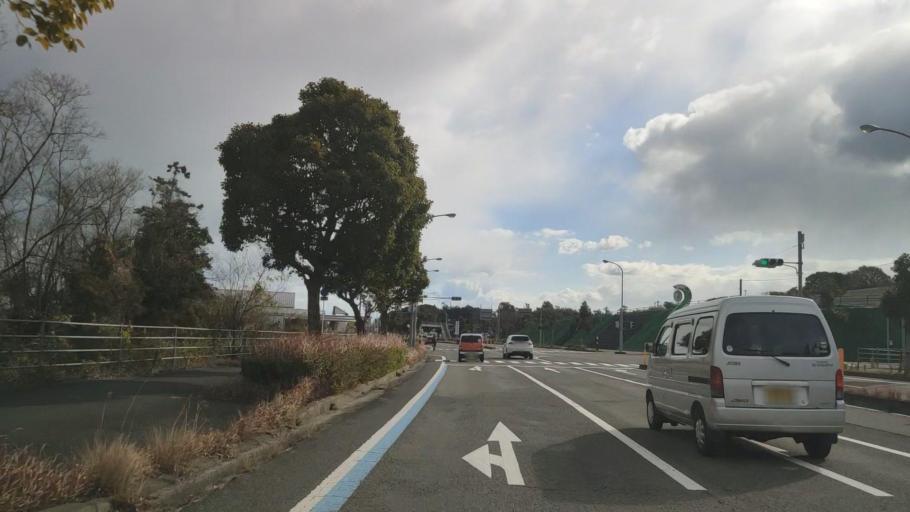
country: JP
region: Ehime
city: Hojo
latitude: 34.0633
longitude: 132.9546
